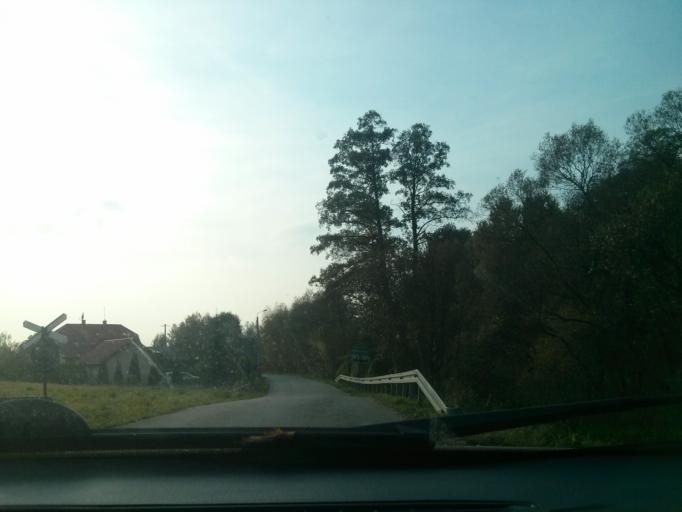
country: PL
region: Masovian Voivodeship
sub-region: Powiat piaseczynski
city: Konstancin-Jeziorna
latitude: 52.1230
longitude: 21.1535
